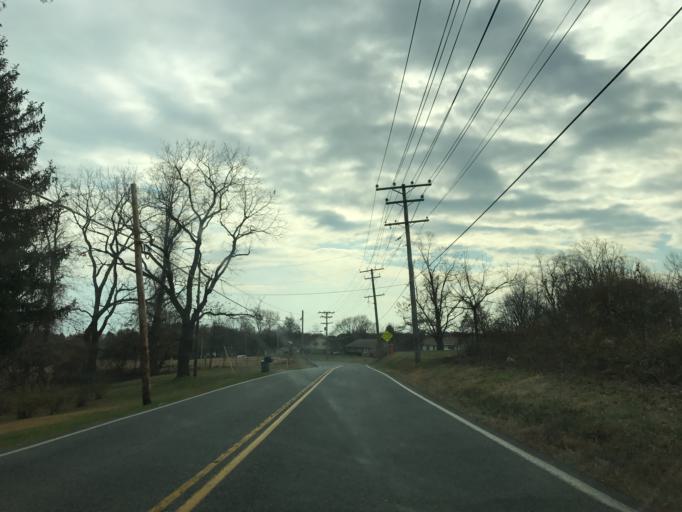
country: US
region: Maryland
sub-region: Harford County
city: Jarrettsville
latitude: 39.5843
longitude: -76.4287
